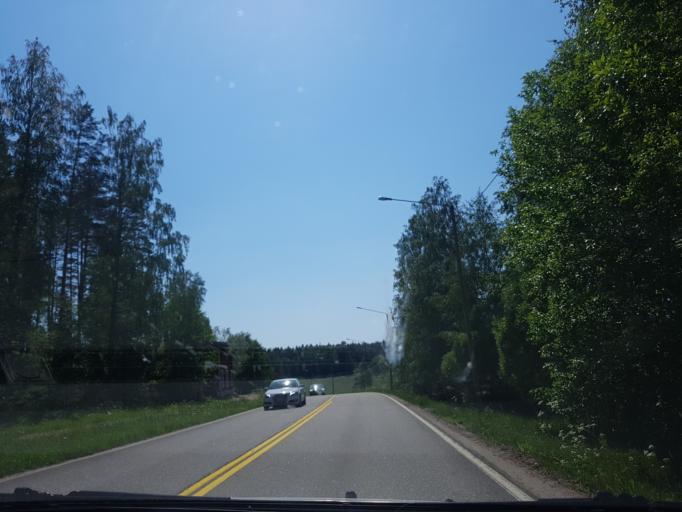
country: FI
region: Uusimaa
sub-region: Helsinki
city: Vihti
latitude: 60.3234
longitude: 24.4050
